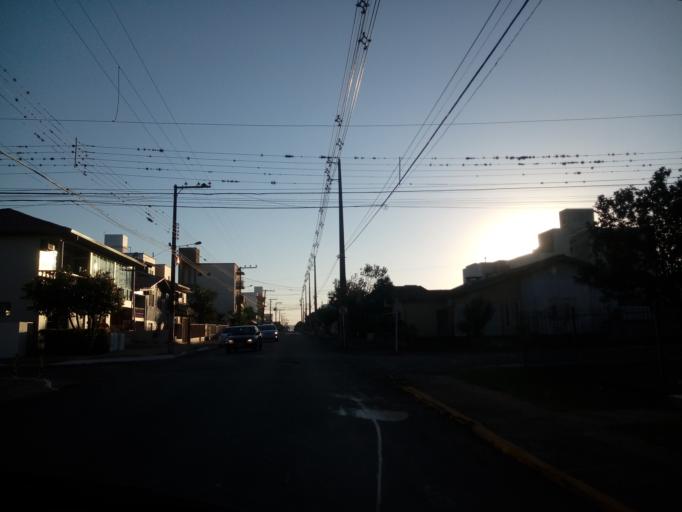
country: BR
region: Santa Catarina
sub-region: Chapeco
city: Chapeco
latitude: -27.0882
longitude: -52.6310
